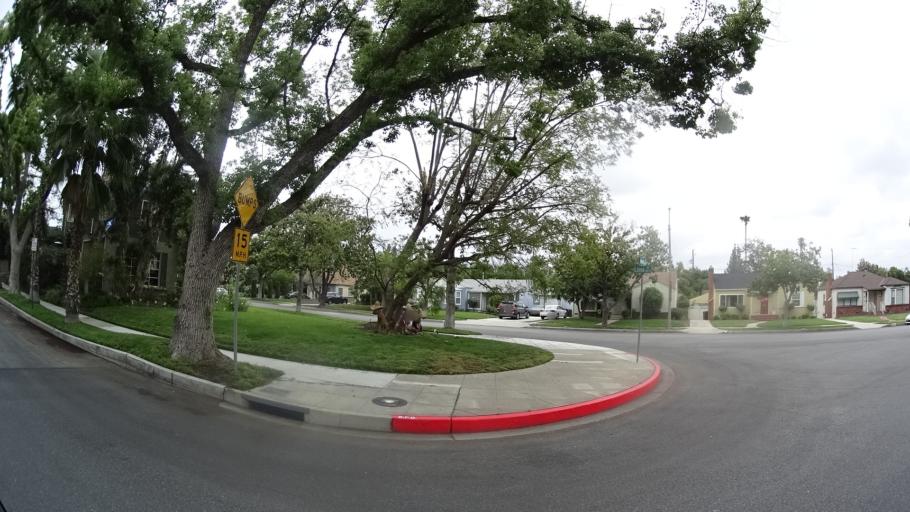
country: US
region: California
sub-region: Los Angeles County
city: Universal City
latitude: 34.1630
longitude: -118.3415
